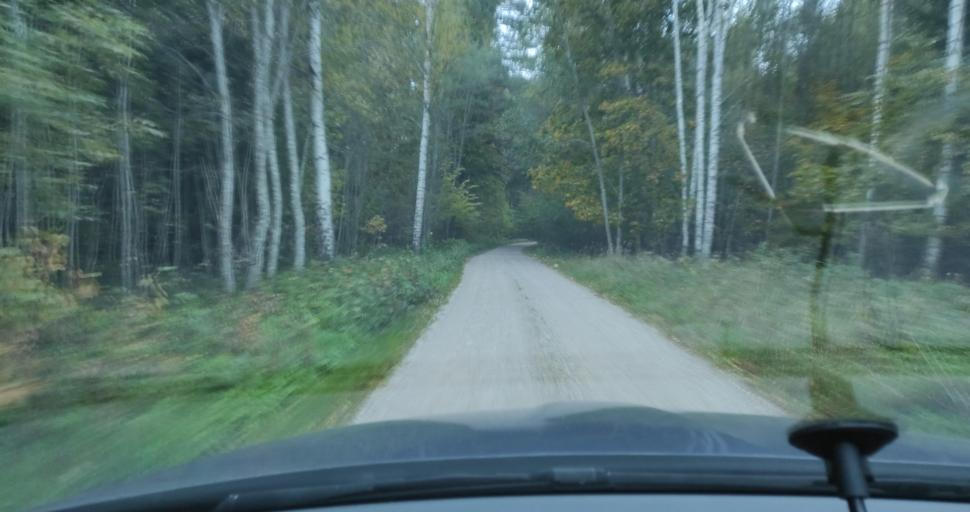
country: LV
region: Kandava
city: Kandava
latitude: 57.0212
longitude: 22.7590
